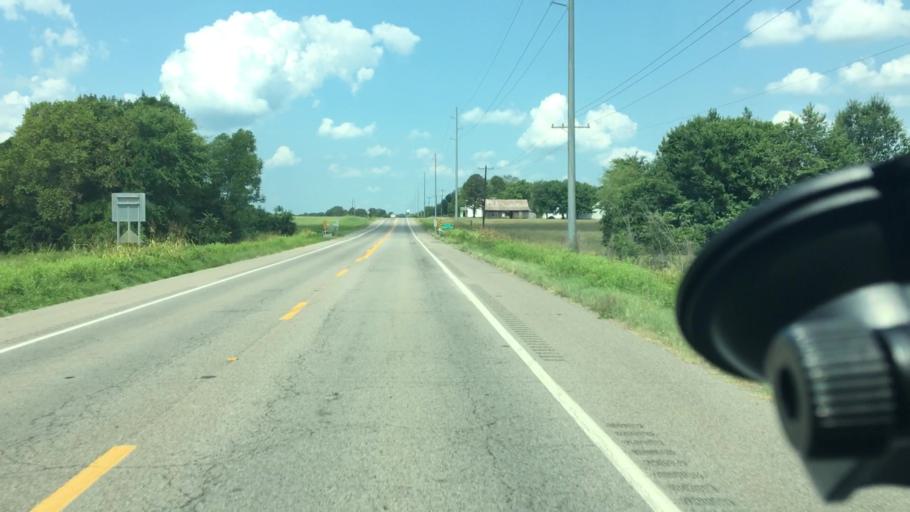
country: US
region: Arkansas
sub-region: Logan County
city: Paris
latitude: 35.2946
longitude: -93.6558
